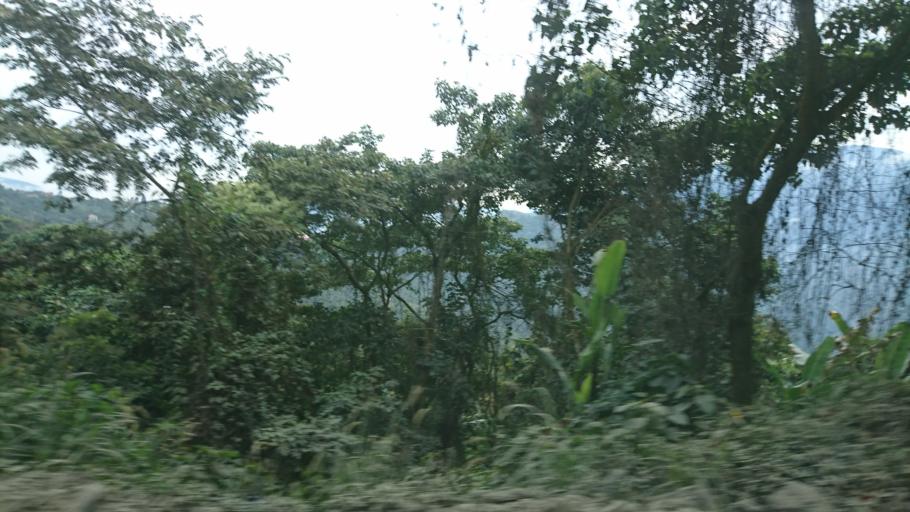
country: BO
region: La Paz
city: Coroico
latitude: -16.1984
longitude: -67.7057
